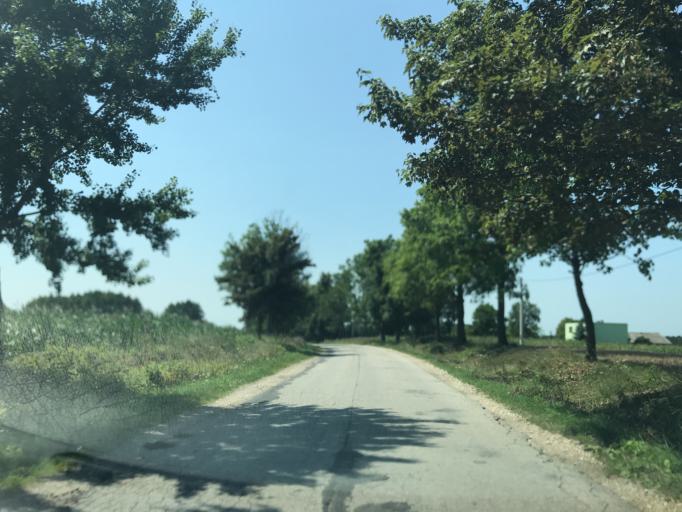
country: PL
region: Kujawsko-Pomorskie
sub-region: Powiat lipnowski
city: Chrostkowo
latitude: 52.9891
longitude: 19.2767
